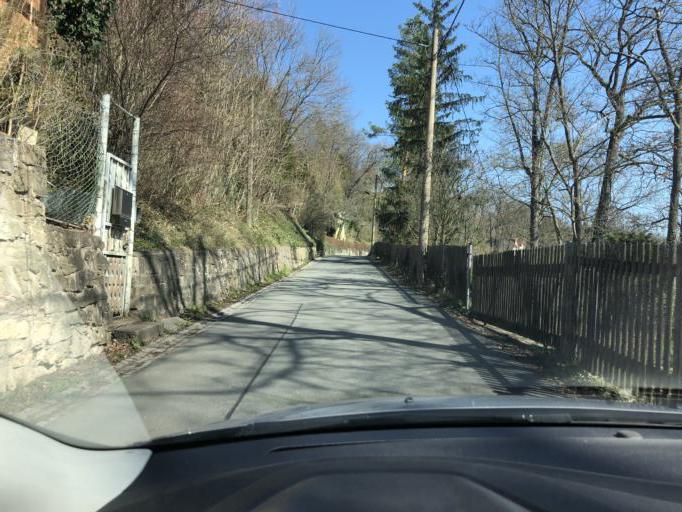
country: DE
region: Thuringia
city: Rudolstadt
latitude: 50.7228
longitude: 11.3319
